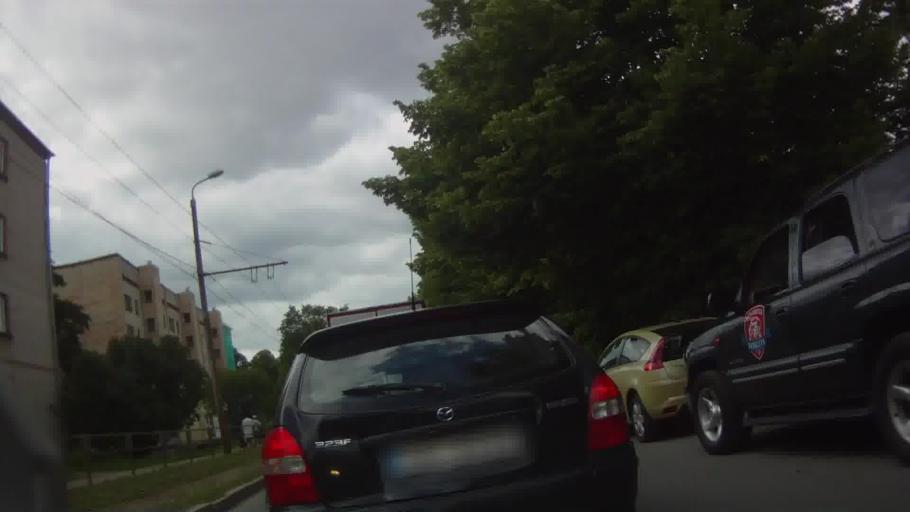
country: LV
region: Riga
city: Riga
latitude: 56.9159
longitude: 24.1097
